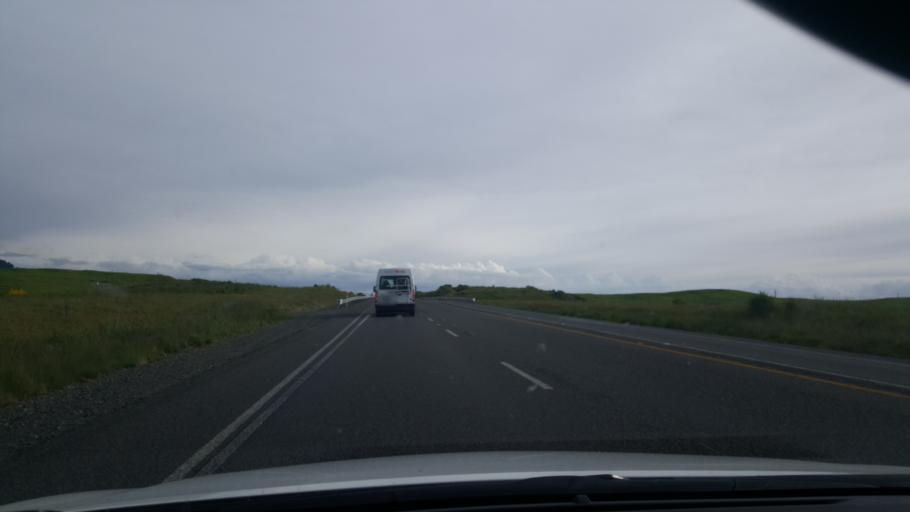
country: NZ
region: Waikato
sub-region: Taupo District
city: Taupo
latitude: -38.6437
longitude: 176.0997
